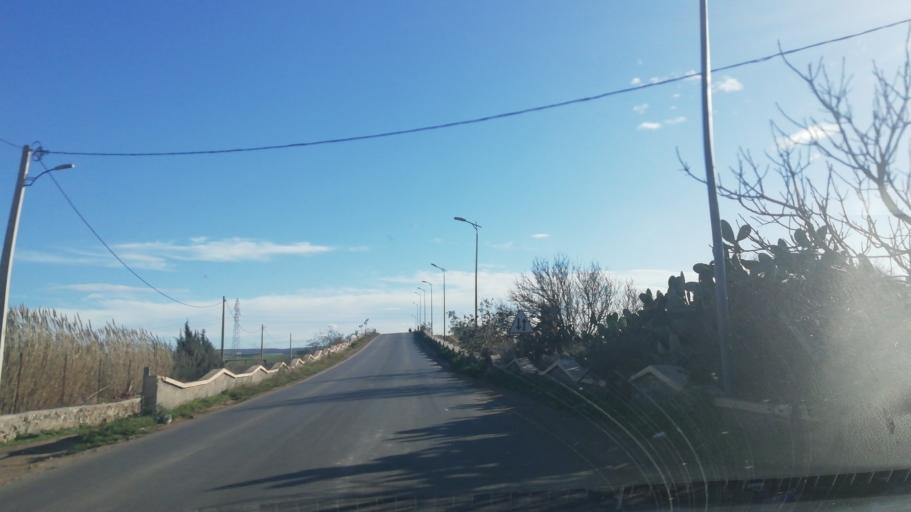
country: DZ
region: Oran
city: Sidi ech Chahmi
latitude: 35.6870
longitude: -0.5046
